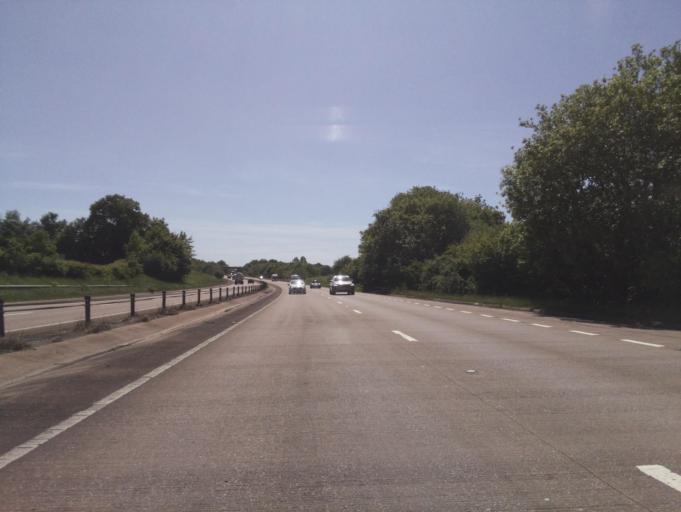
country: GB
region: England
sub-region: Devon
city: Newton Poppleford
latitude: 50.7419
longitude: -3.3624
